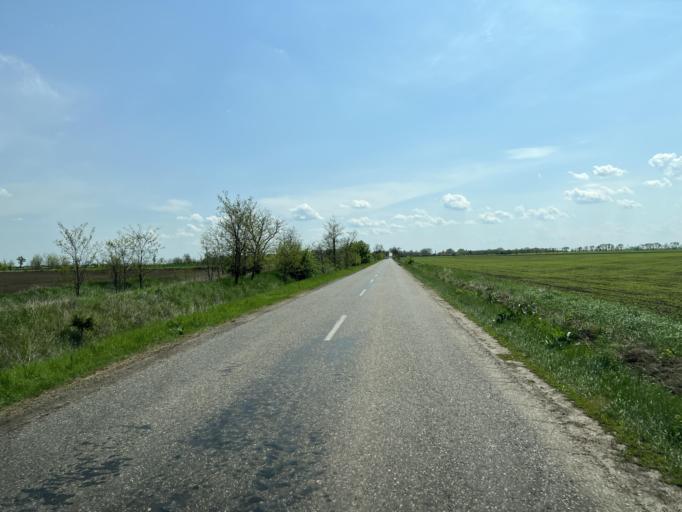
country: HU
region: Pest
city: Tapioszentmarton
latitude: 47.2666
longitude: 19.7703
